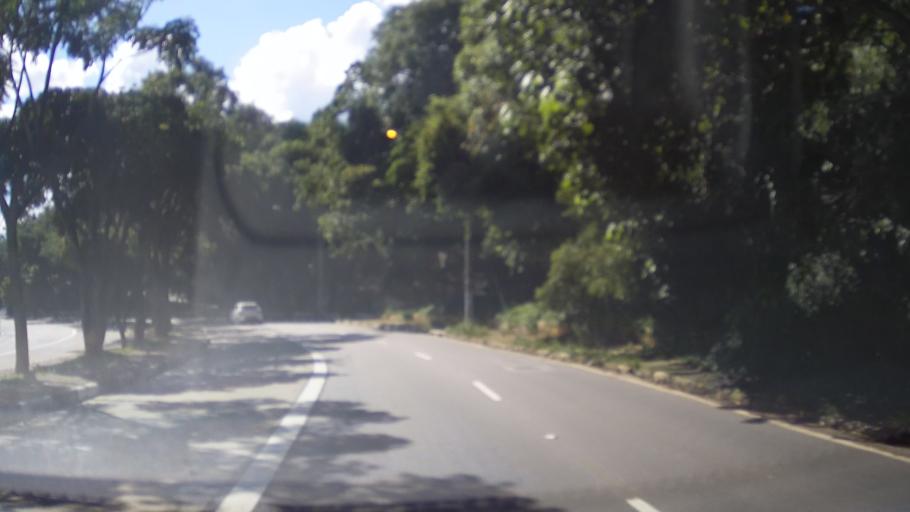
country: BR
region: Sao Paulo
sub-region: Guarulhos
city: Guarulhos
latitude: -23.4555
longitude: -46.5514
